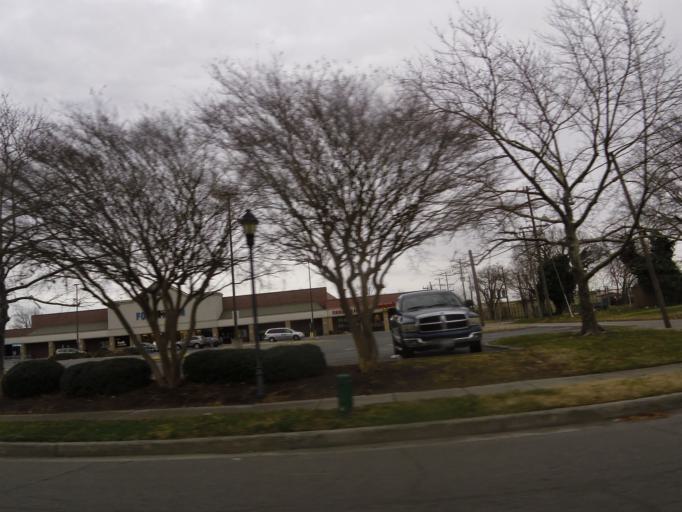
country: US
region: Virginia
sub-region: City of Portsmouth
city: Portsmouth
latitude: 36.8359
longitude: -76.3184
